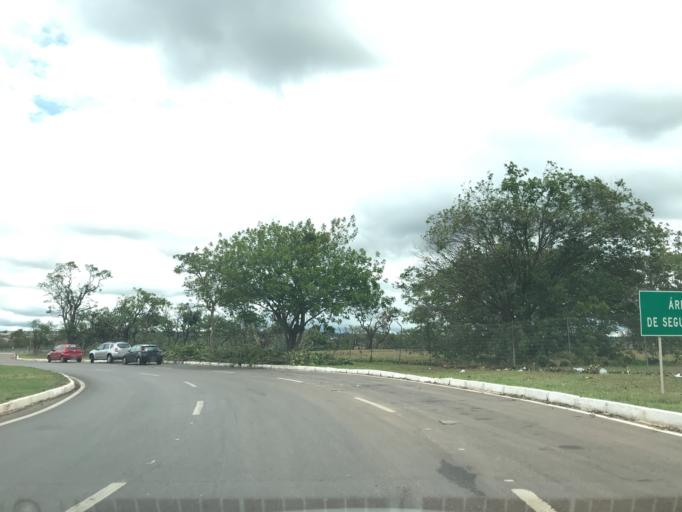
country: BR
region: Federal District
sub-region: Brasilia
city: Brasilia
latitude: -15.7911
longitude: -47.8296
